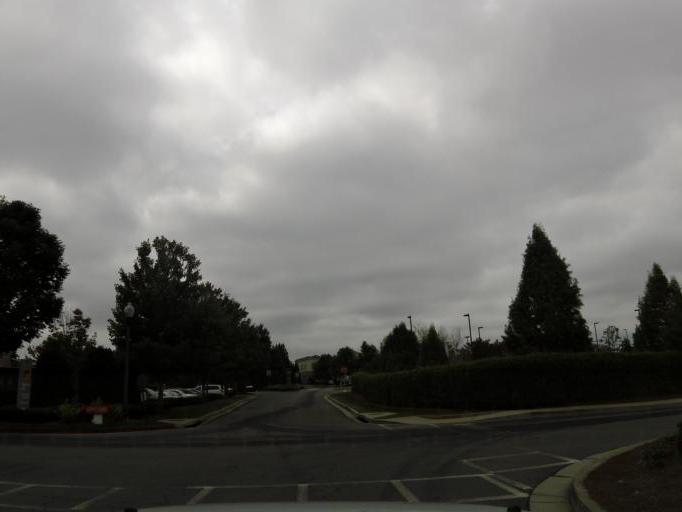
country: US
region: Georgia
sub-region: Cobb County
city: Kennesaw
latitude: 34.0375
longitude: -84.5694
